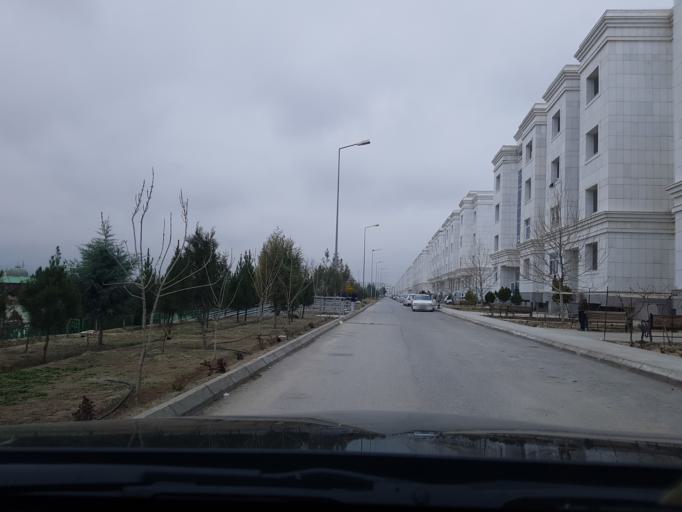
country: TM
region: Ahal
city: Abadan
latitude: 38.1633
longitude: 57.9388
